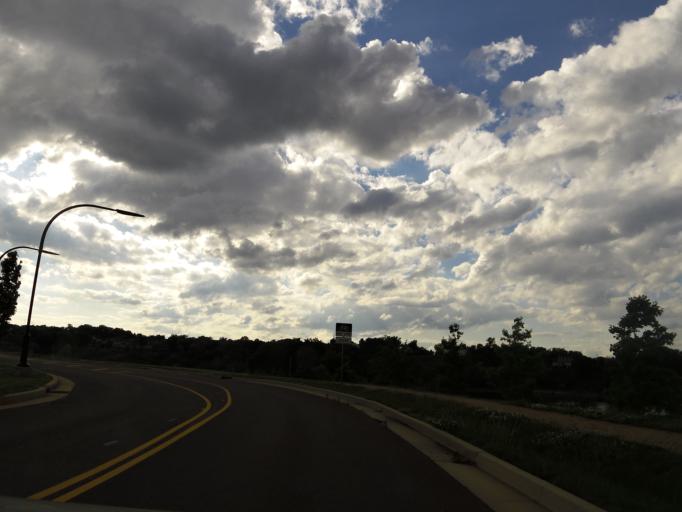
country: US
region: Tennessee
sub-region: Knox County
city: Knoxville
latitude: 35.9463
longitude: -83.9497
